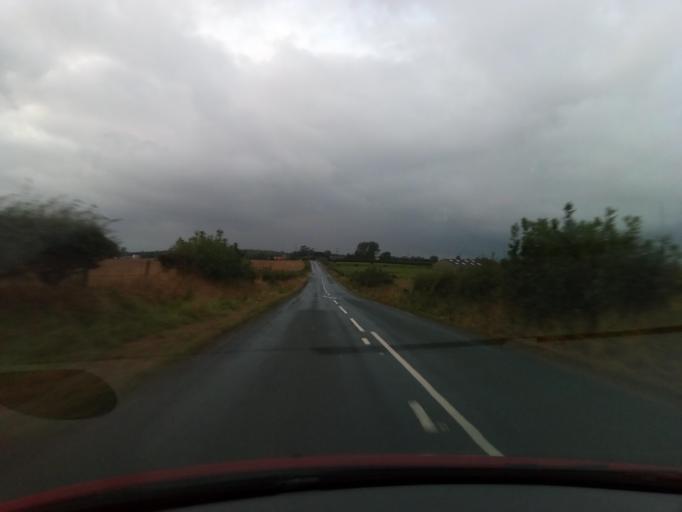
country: GB
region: England
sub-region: Darlington
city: Summerhouse
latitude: 54.6021
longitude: -1.6805
